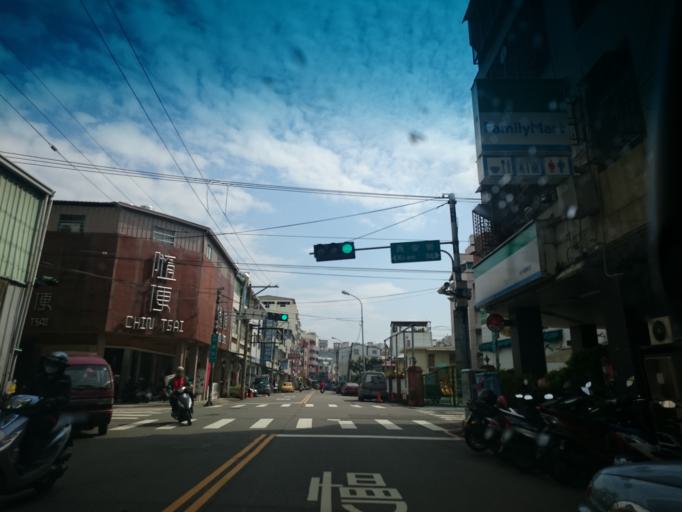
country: TW
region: Taiwan
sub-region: Taichung City
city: Taichung
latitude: 24.1818
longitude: 120.6425
